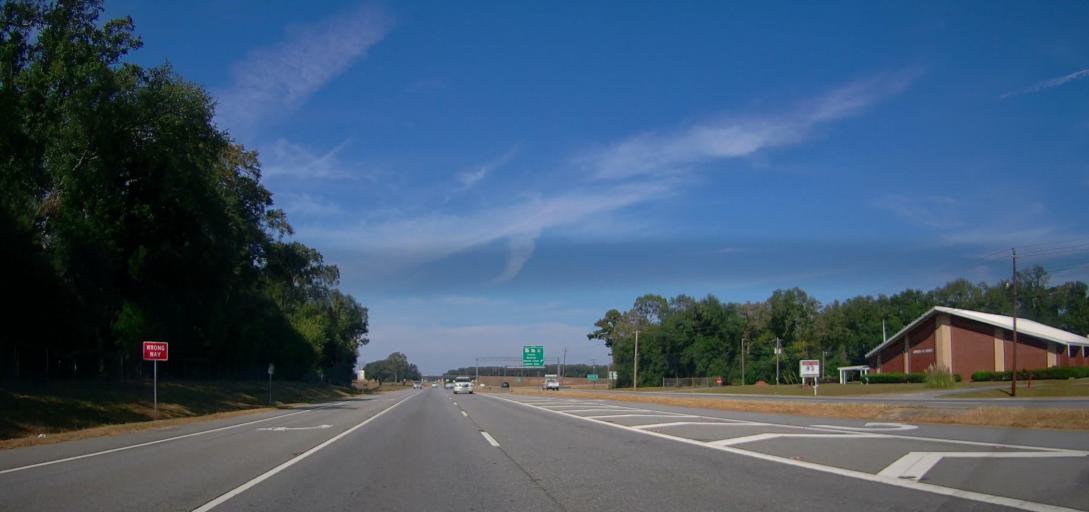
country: US
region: Georgia
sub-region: Dougherty County
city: Albany
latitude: 31.5396
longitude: -84.1153
